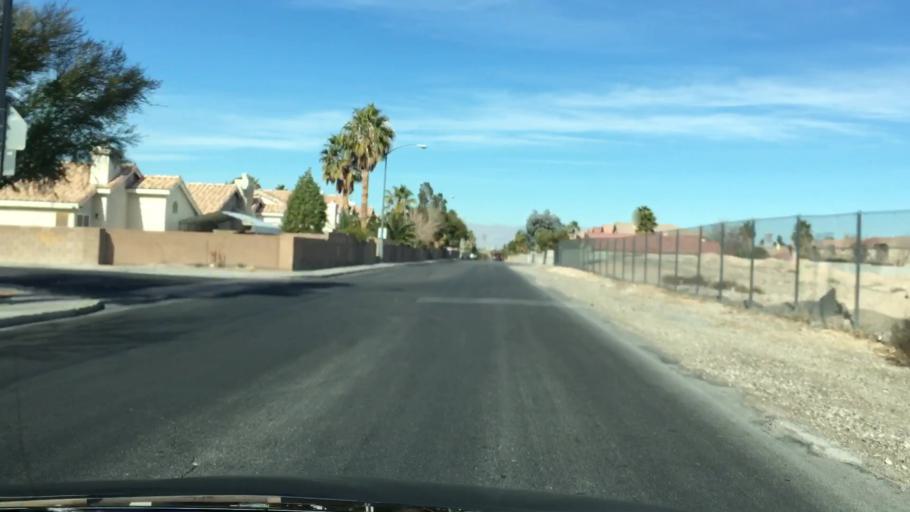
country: US
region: Nevada
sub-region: Clark County
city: Paradise
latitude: 36.0359
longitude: -115.1407
